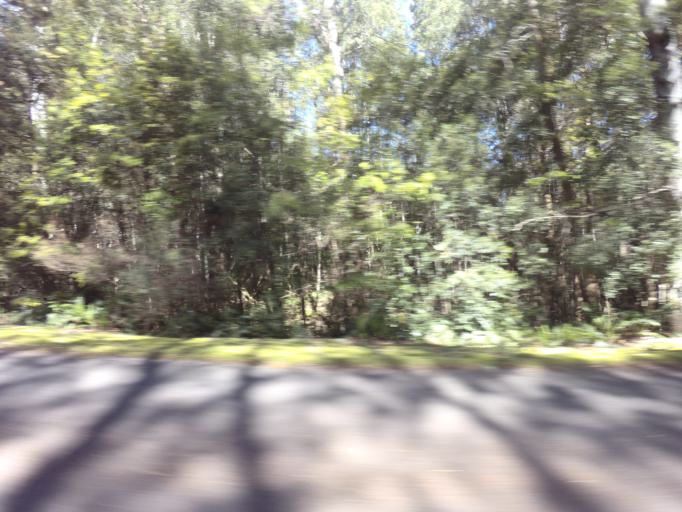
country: AU
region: Tasmania
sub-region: Huon Valley
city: Geeveston
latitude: -42.8279
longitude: 146.3228
